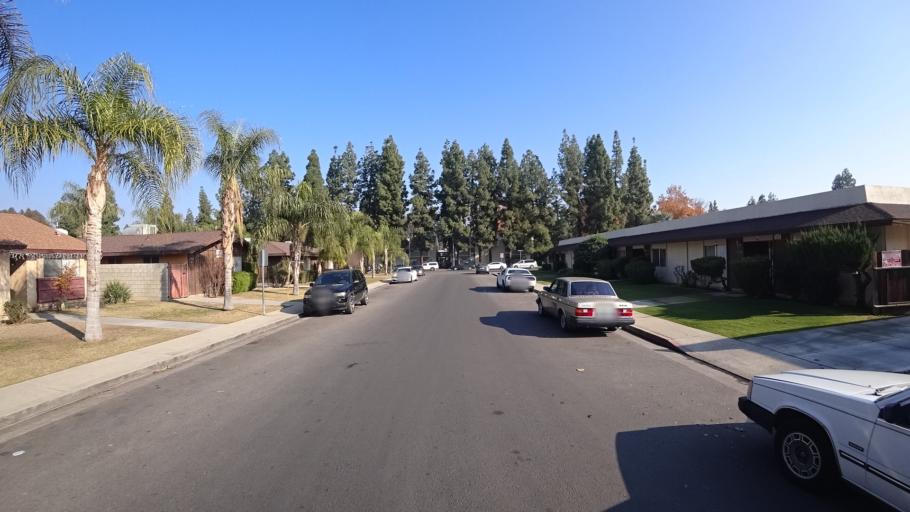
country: US
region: California
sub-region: Kern County
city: Bakersfield
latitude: 35.3482
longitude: -119.0597
